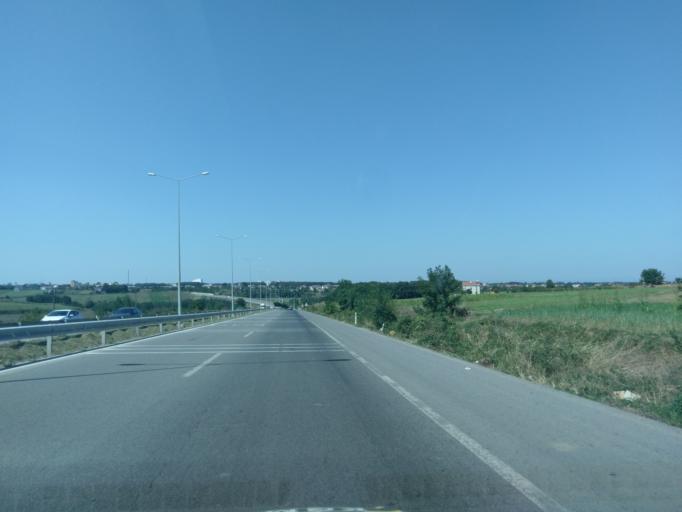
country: TR
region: Samsun
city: Bafra
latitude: 41.5330
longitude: 35.9498
